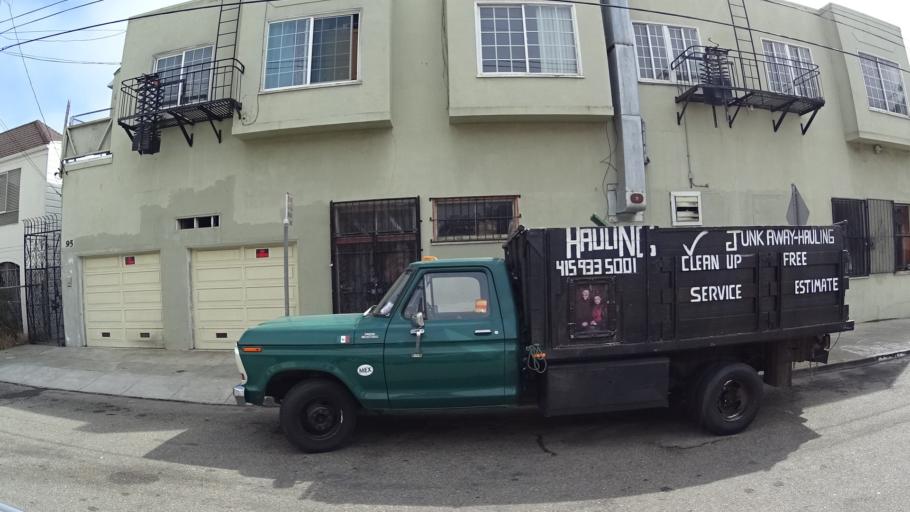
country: US
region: California
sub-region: San Mateo County
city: Brisbane
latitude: 37.7089
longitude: -122.4208
